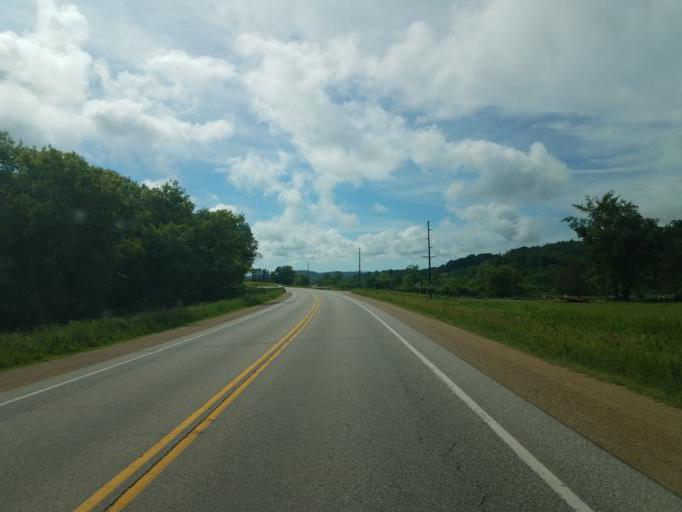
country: US
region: Wisconsin
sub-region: Monroe County
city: Tomah
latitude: 43.8230
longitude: -90.4424
